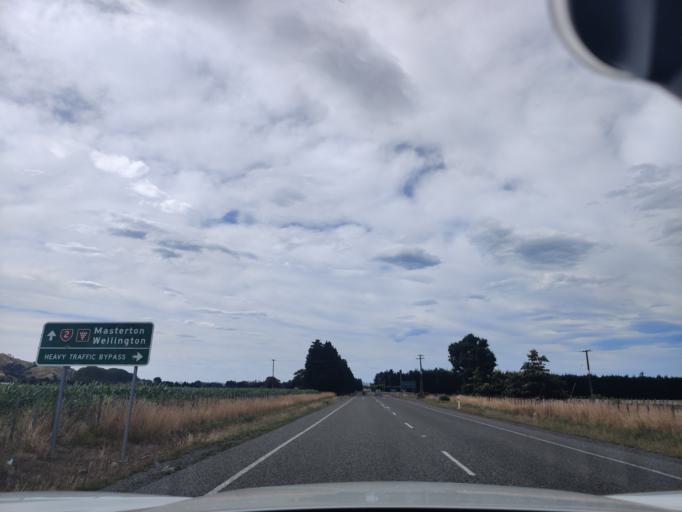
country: NZ
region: Wellington
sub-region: Masterton District
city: Masterton
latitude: -40.8569
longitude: 175.6397
